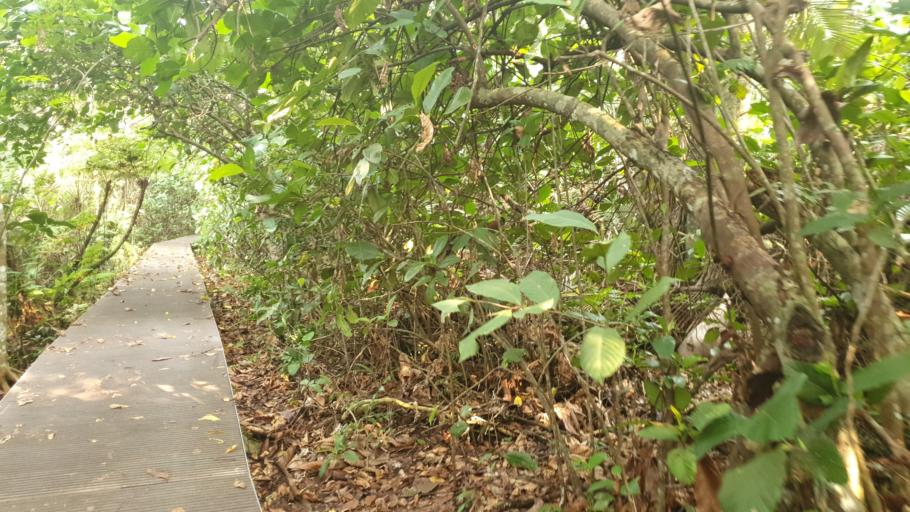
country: SG
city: Singapore
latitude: 1.3490
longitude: 103.8088
